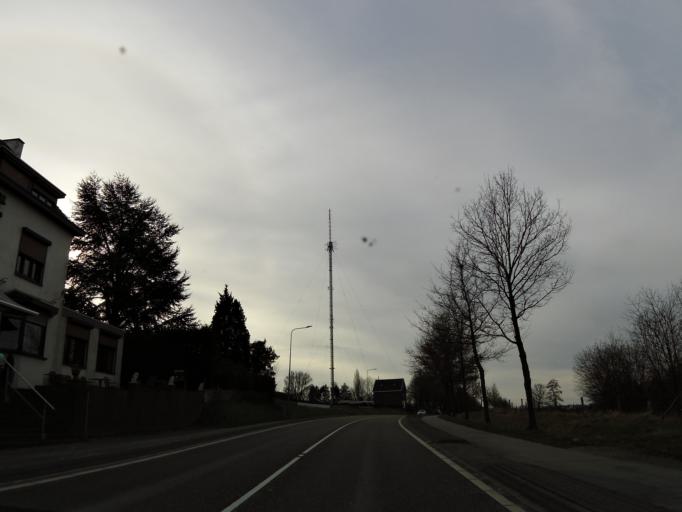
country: NL
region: Limburg
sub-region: Valkenburg aan de Geul
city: Valkenburg
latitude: 50.8771
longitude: 5.8476
